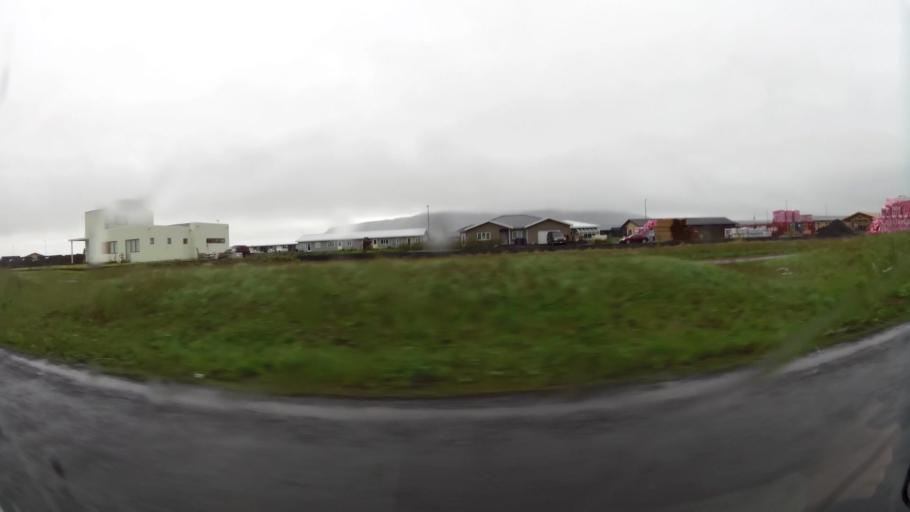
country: IS
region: South
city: Selfoss
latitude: 63.9239
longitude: -20.9838
